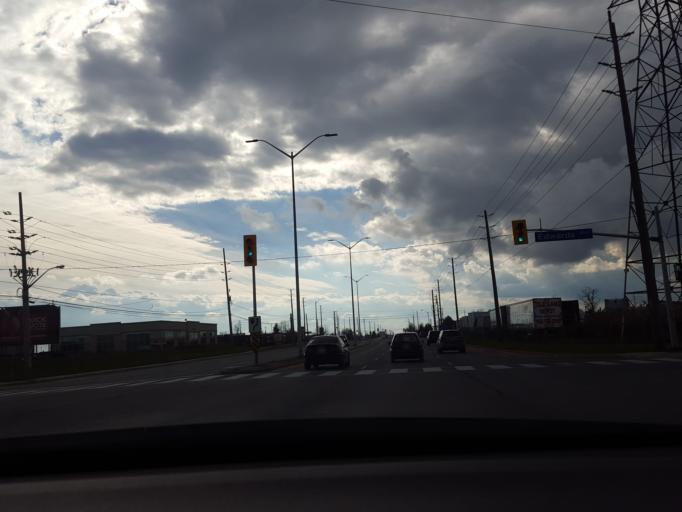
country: CA
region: Ontario
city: Brampton
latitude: 43.6488
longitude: -79.7032
